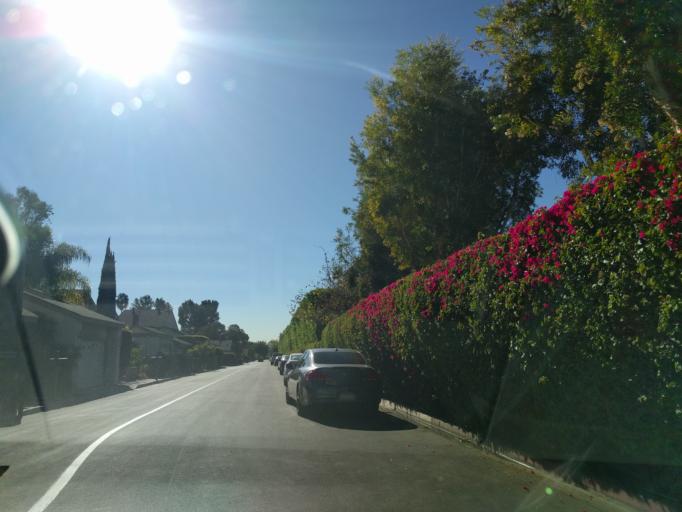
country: US
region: California
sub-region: Orange County
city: Irvine
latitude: 33.7071
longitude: -117.7823
